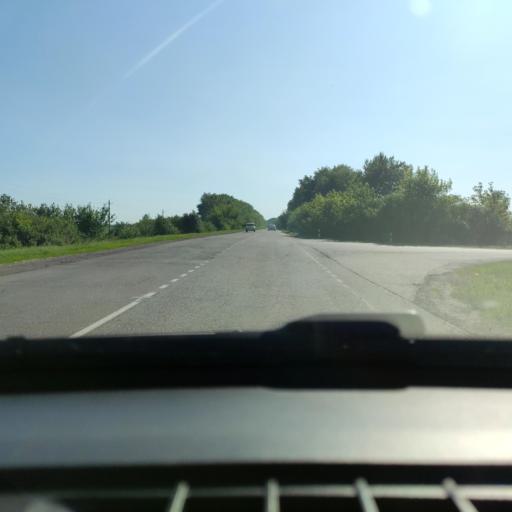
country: RU
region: Voronezj
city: Panino
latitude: 51.6249
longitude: 40.0362
